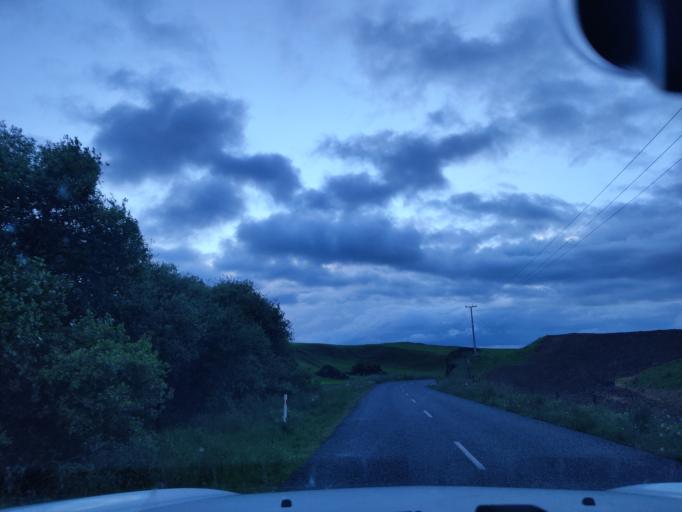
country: NZ
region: Waikato
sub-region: South Waikato District
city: Tokoroa
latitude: -38.1763
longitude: 175.7767
